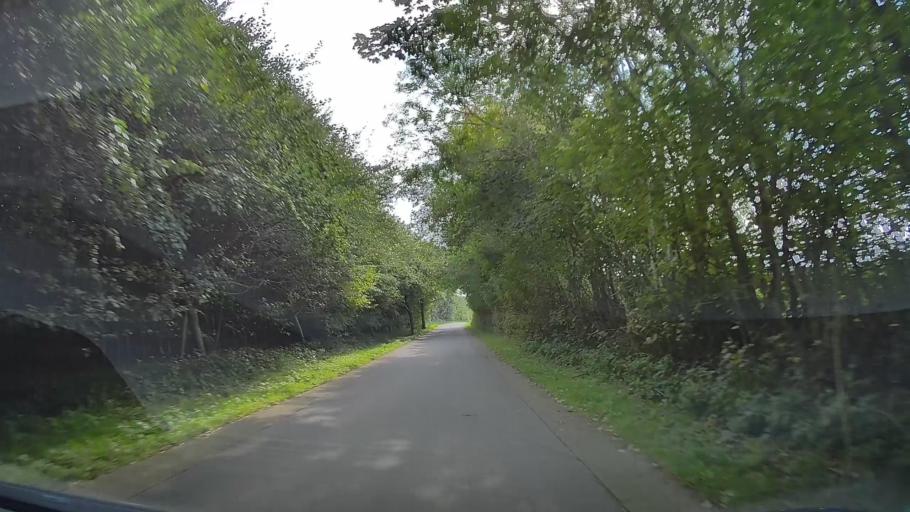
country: DE
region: Schleswig-Holstein
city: Ringsberg
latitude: 54.8250
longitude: 9.6044
